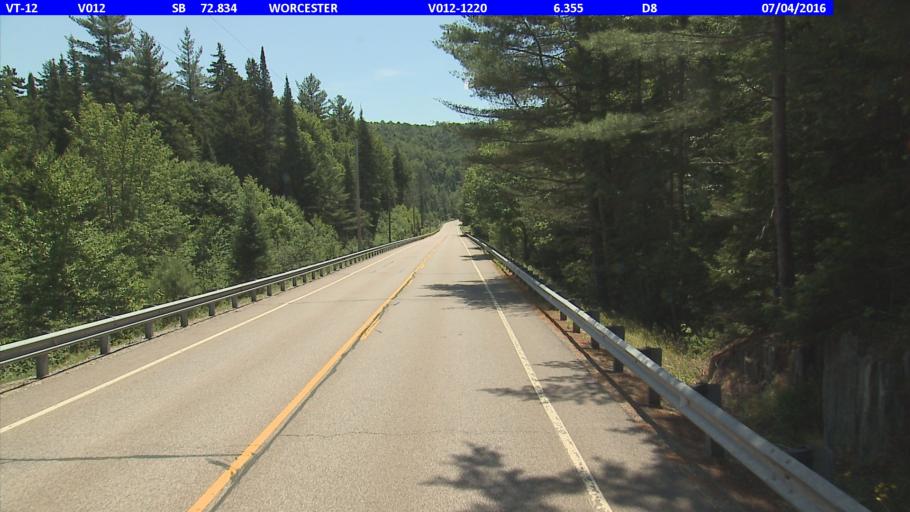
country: US
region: Vermont
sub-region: Lamoille County
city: Morrisville
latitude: 44.4330
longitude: -72.5348
